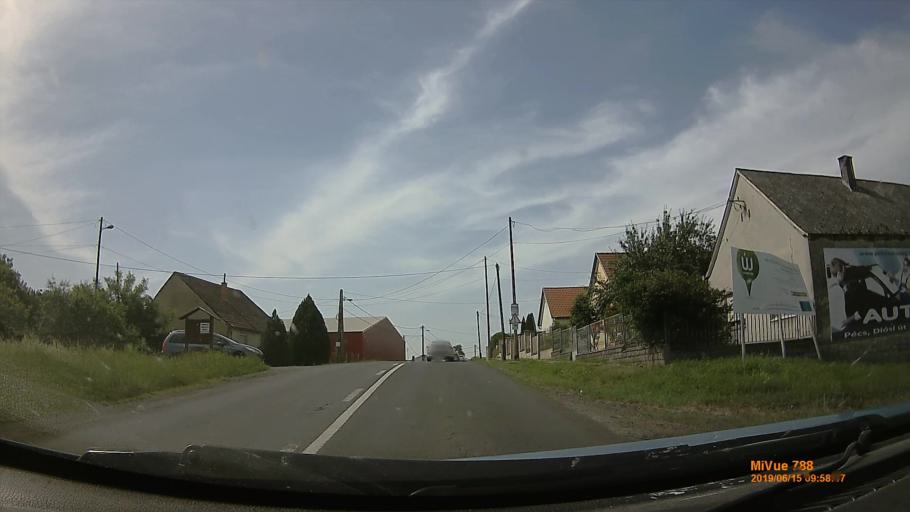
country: HU
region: Baranya
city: Sasd
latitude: 46.2258
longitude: 18.1218
